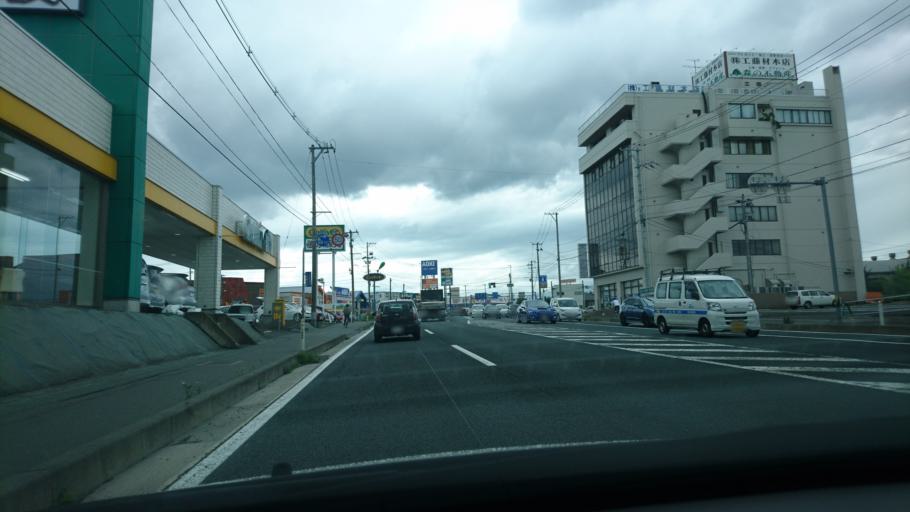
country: JP
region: Iwate
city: Morioka-shi
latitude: 39.7249
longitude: 141.1263
